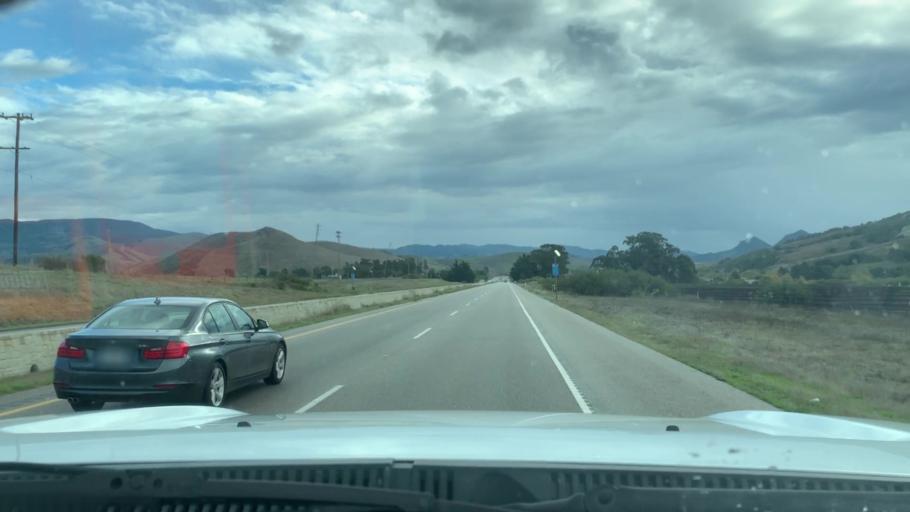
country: US
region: California
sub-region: San Luis Obispo County
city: Morro Bay
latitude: 35.3574
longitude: -120.7953
